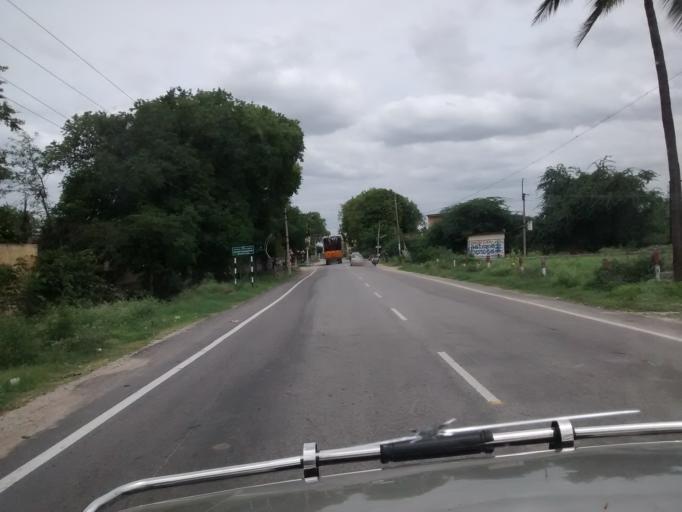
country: IN
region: Andhra Pradesh
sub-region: Chittoor
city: Chittoor
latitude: 13.2872
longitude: 79.0396
